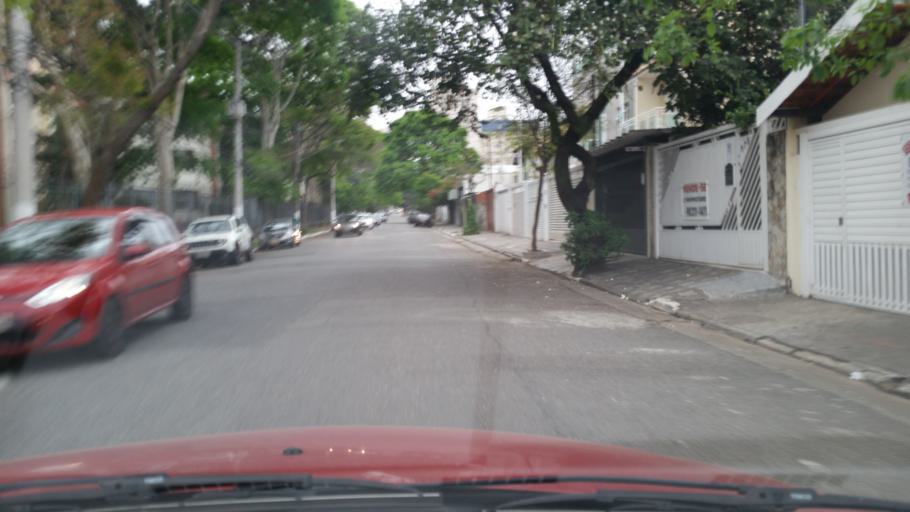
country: BR
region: Sao Paulo
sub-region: Sao Paulo
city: Sao Paulo
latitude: -23.5970
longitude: -46.6240
